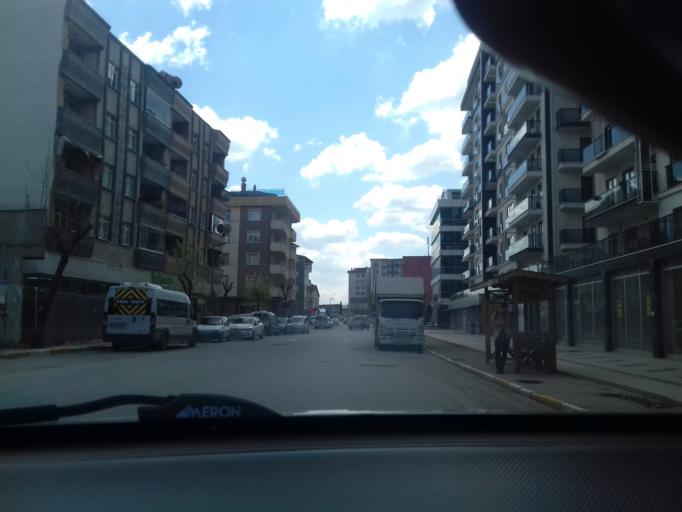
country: TR
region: Istanbul
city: Pendik
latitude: 40.8923
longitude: 29.2773
